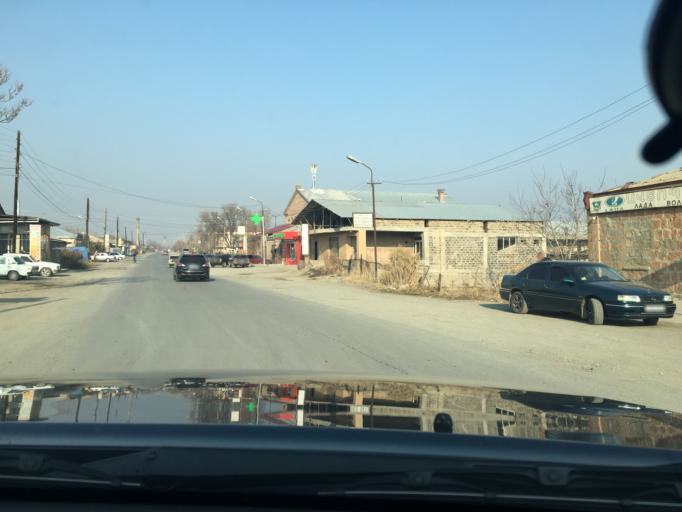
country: AM
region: Armavir
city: Aygeshat
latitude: 40.0834
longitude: 44.0528
